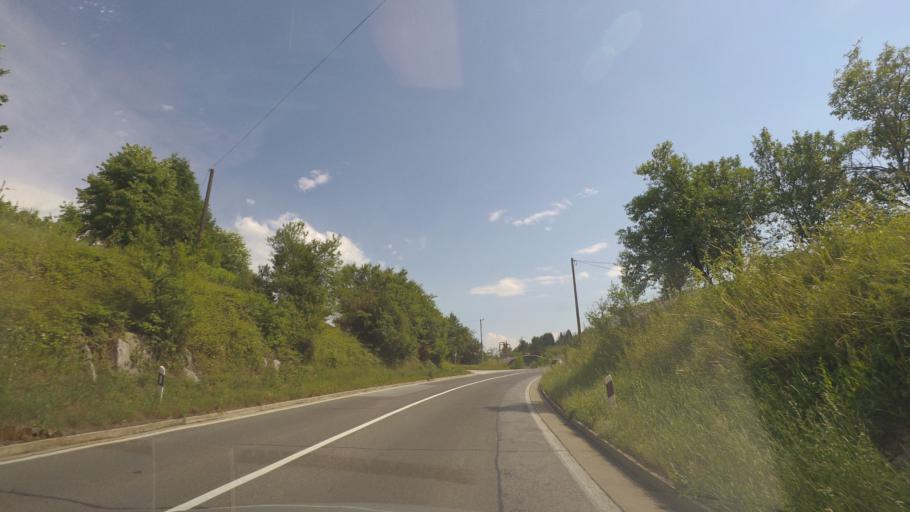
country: HR
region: Karlovacka
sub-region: Grad Karlovac
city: Karlovac
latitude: 45.4500
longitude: 15.4930
